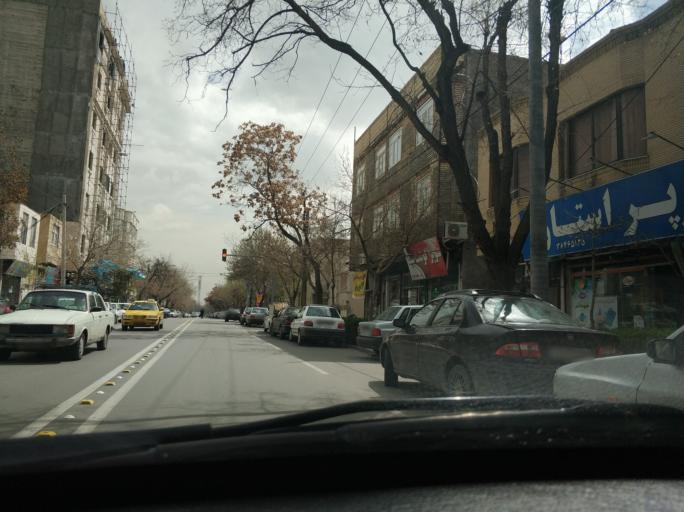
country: IR
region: Razavi Khorasan
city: Mashhad
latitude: 36.2799
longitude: 59.5739
